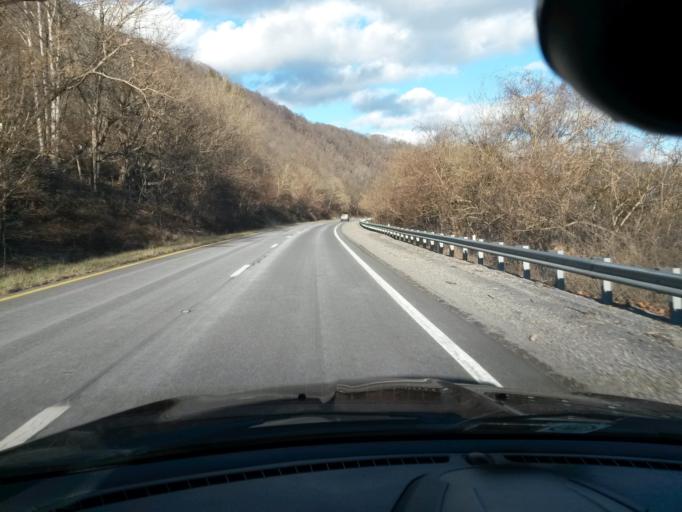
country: US
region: Virginia
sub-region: Giles County
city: Narrows
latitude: 37.3819
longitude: -80.8458
